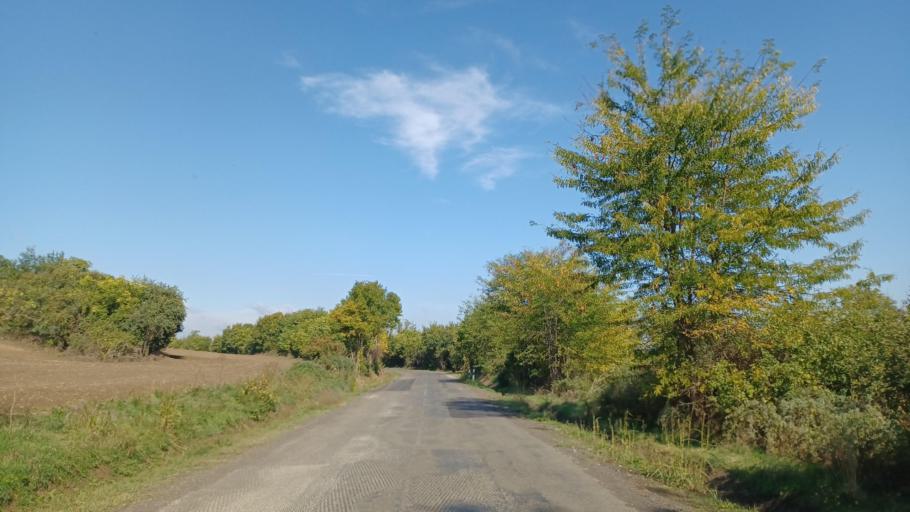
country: HU
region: Tolna
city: Nagydorog
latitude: 46.5967
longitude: 18.5956
